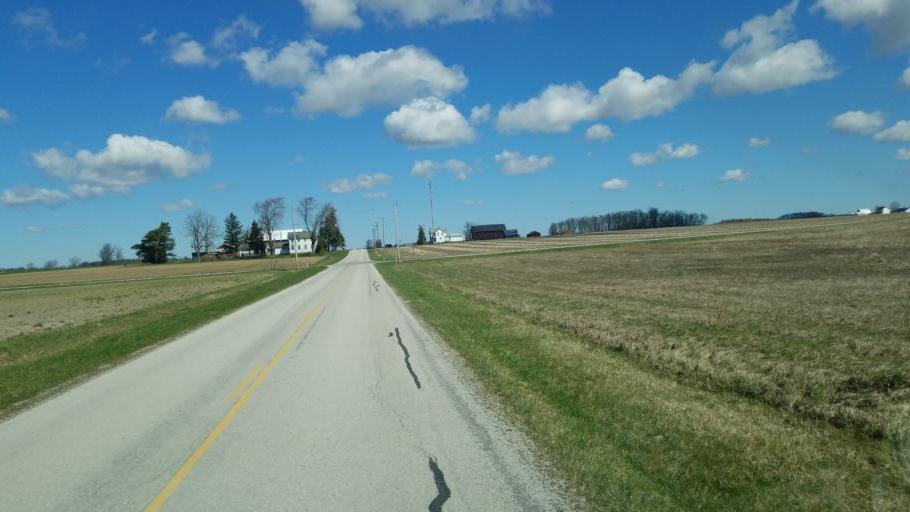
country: US
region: Ohio
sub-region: Sandusky County
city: Mount Carmel
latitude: 41.1894
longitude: -82.9377
